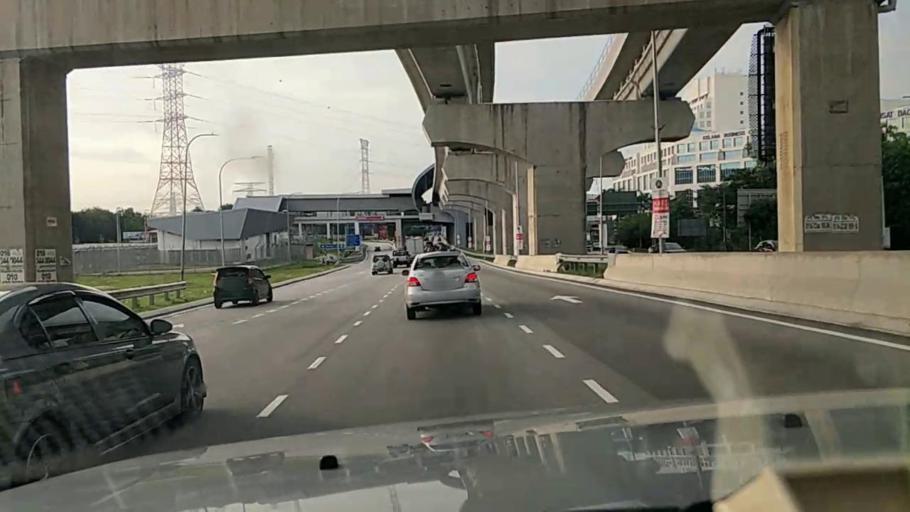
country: MY
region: Selangor
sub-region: Petaling
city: Petaling Jaya
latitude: 3.0941
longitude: 101.5911
